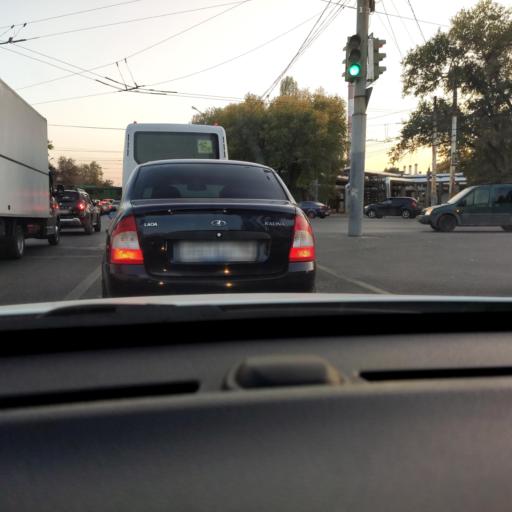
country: RU
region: Voronezj
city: Voronezh
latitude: 51.6311
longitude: 39.2312
